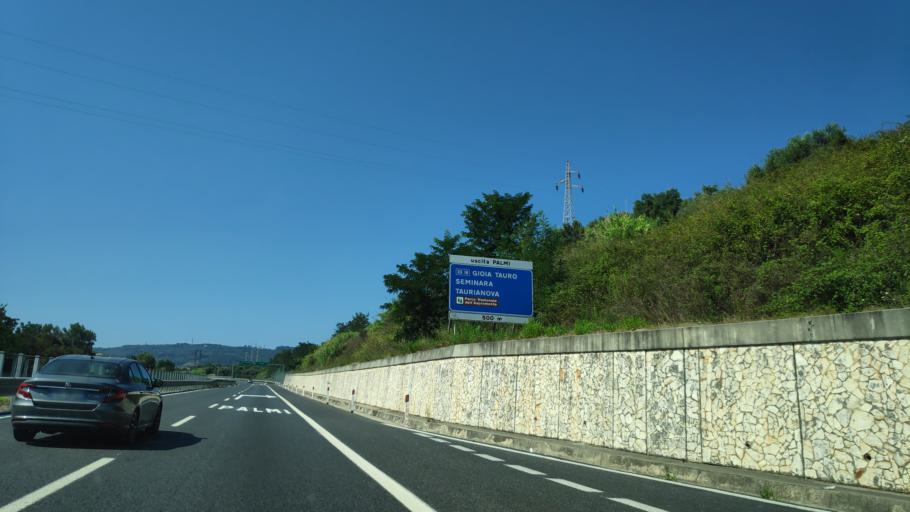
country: IT
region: Calabria
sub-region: Provincia di Reggio Calabria
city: Palmi
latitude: 38.3732
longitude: 15.8685
